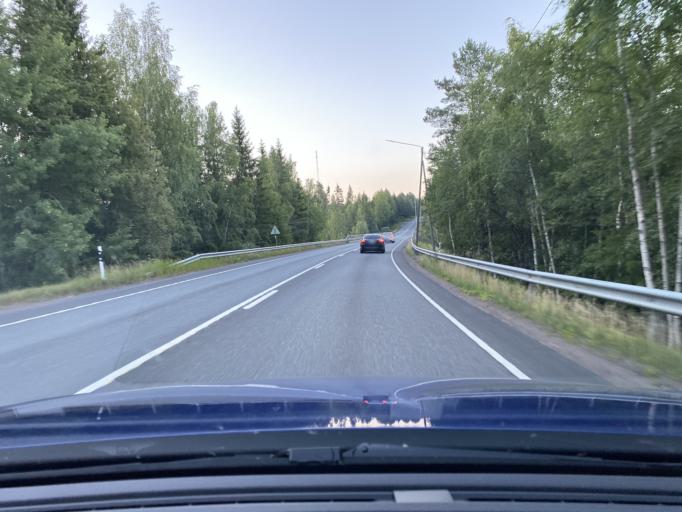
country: FI
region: Pirkanmaa
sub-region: Luoteis-Pirkanmaa
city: Ikaalinen
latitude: 61.8493
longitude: 22.9313
